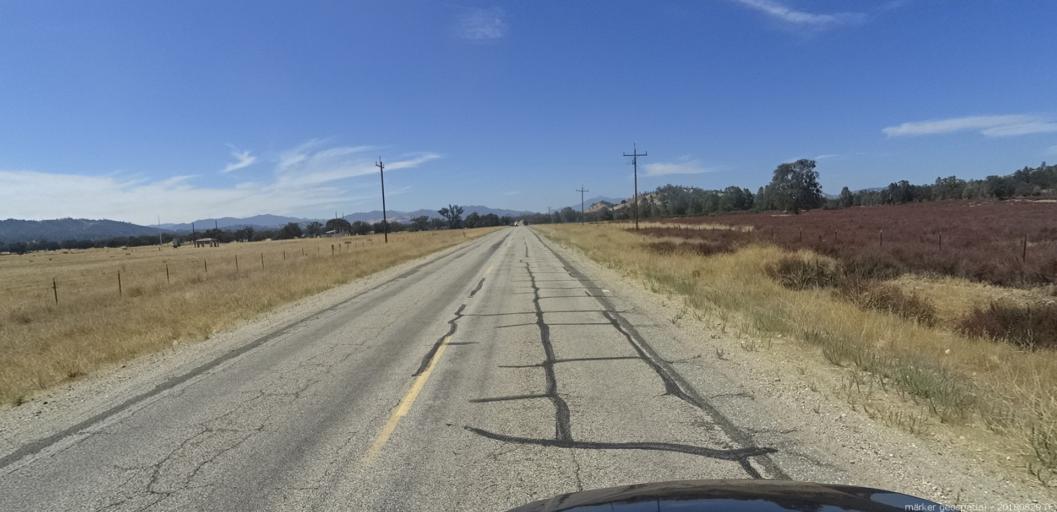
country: US
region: California
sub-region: Monterey County
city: King City
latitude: 35.9622
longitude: -121.1652
